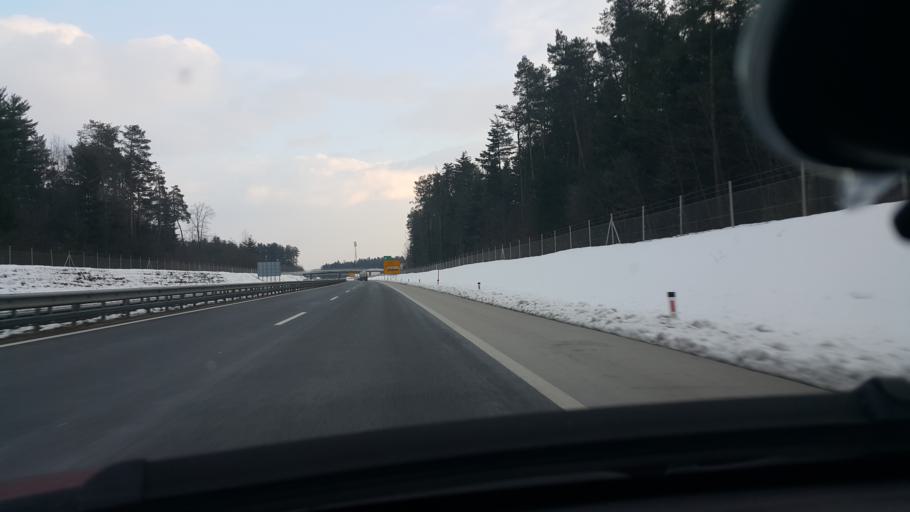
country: SI
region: Kidricevo
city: Kidricevo
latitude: 46.4184
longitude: 15.8037
